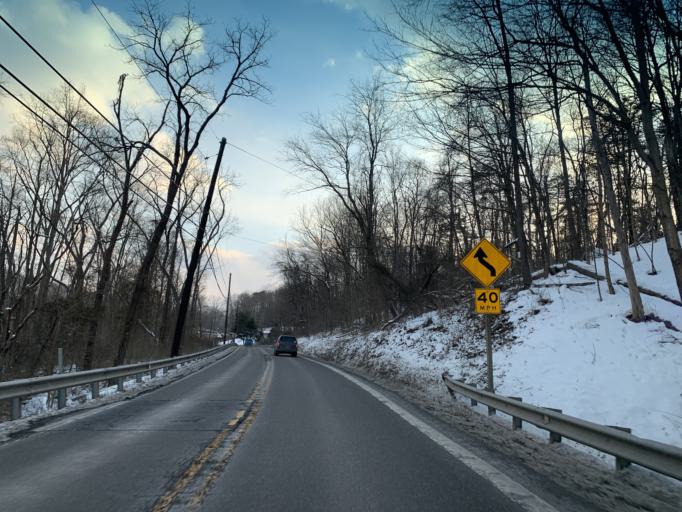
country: US
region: Maryland
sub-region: Allegany County
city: Cumberland
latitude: 39.7109
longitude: -78.7811
